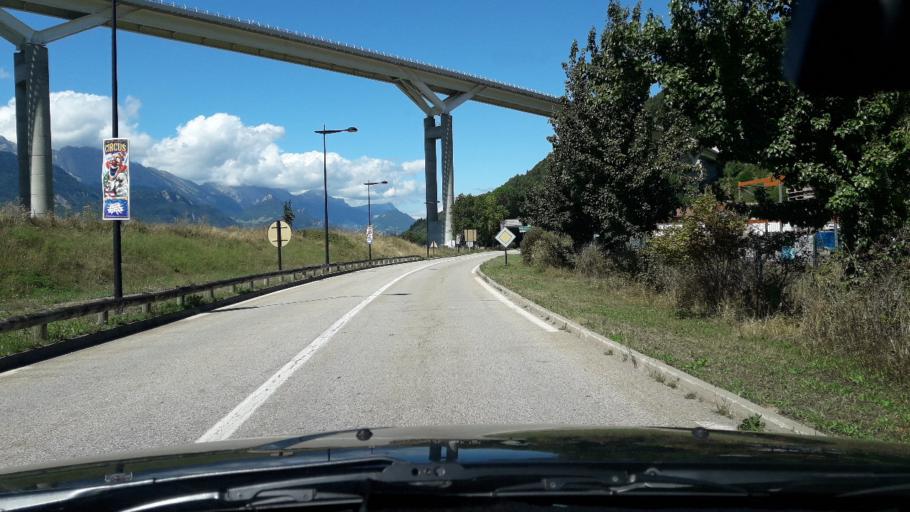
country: FR
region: Rhone-Alpes
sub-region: Departement de l'Isere
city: La Motte-Saint-Martin
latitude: 44.9298
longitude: 5.6395
